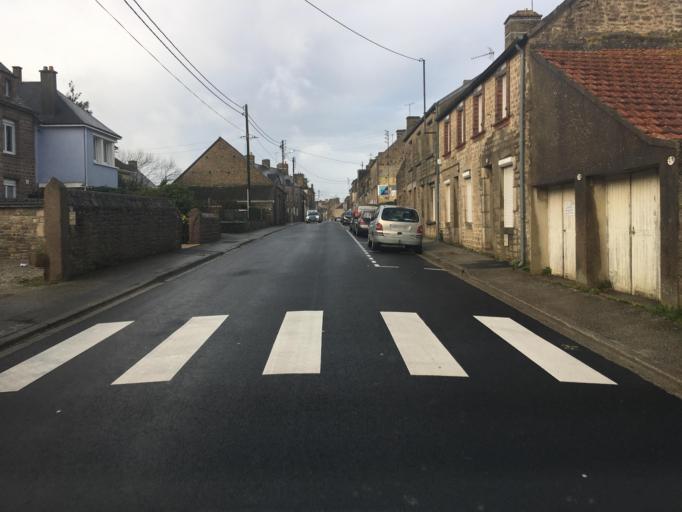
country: FR
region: Lower Normandy
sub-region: Departement de la Manche
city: Saint-Pierre-Eglise
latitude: 49.6670
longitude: -1.3999
